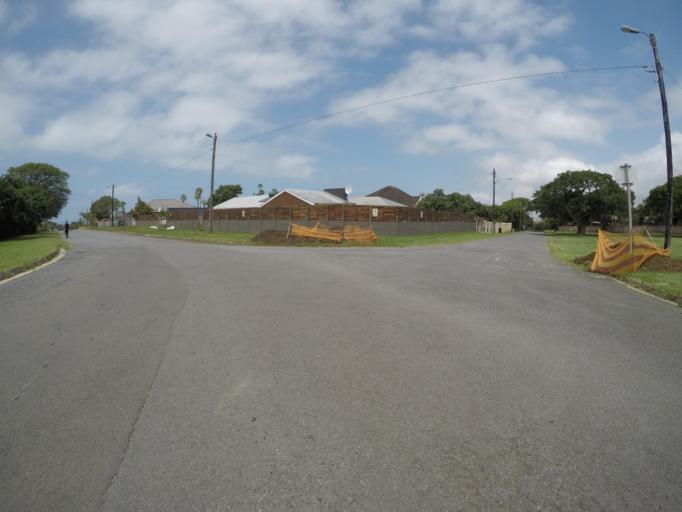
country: ZA
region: Eastern Cape
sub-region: Buffalo City Metropolitan Municipality
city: East London
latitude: -32.9370
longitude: 28.0047
